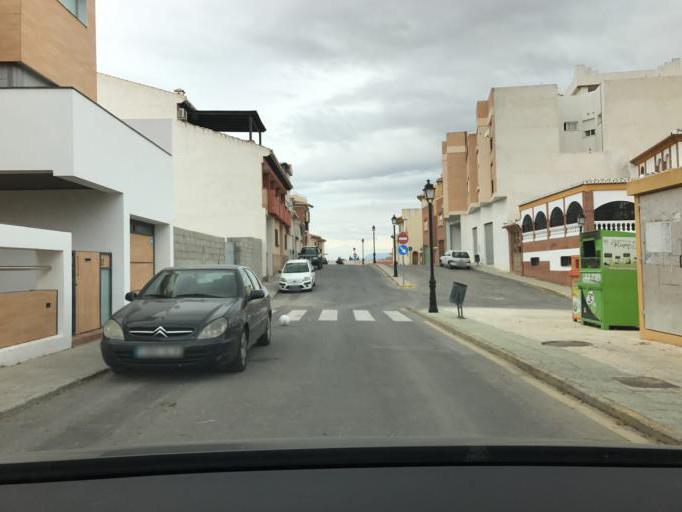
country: ES
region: Andalusia
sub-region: Provincia de Granada
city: Las Gabias
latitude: 37.1291
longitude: -3.6753
